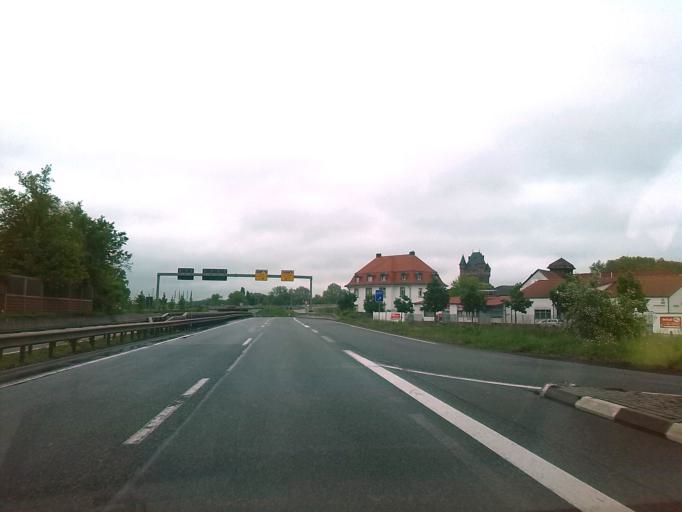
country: DE
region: Rheinland-Pfalz
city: Worms
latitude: 49.6271
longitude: 8.3741
